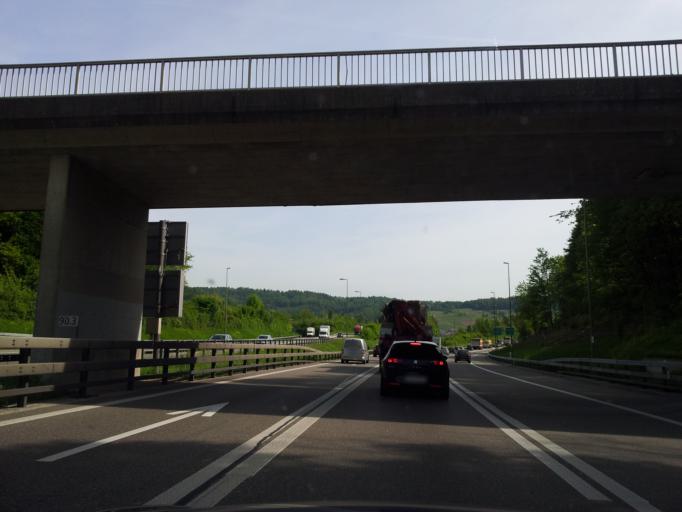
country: CH
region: Zurich
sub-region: Bezirk Dietikon
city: Dietikon / Schoenenwerd
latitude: 47.4083
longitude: 8.4246
